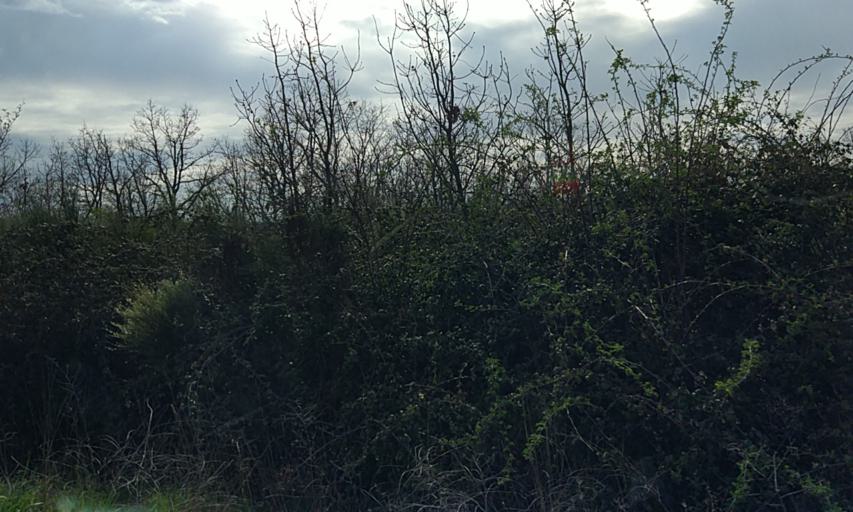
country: ES
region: Castille and Leon
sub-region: Provincia de Salamanca
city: Robleda
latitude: 40.4251
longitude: -6.6021
